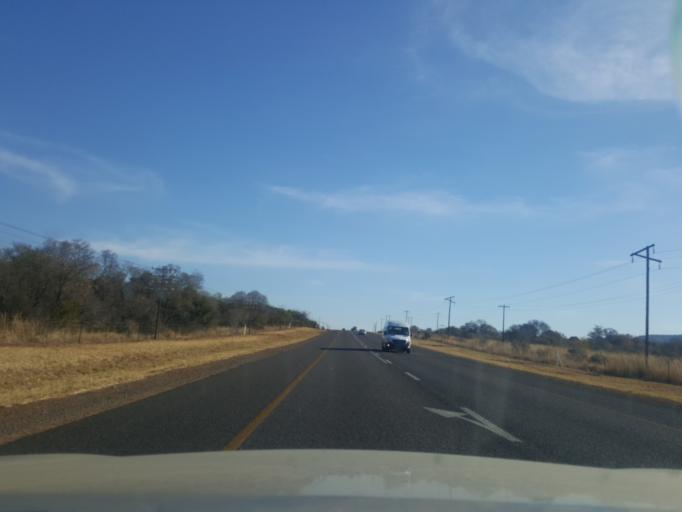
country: ZA
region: North-West
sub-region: Ngaka Modiri Molema District Municipality
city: Zeerust
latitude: -25.5240
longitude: 26.1551
